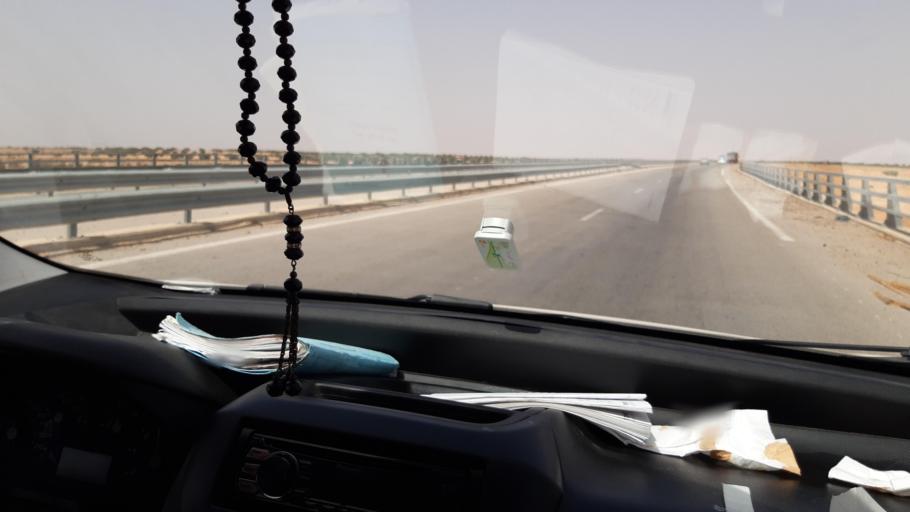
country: TN
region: Safaqis
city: Skhira
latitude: 34.5175
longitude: 10.0780
